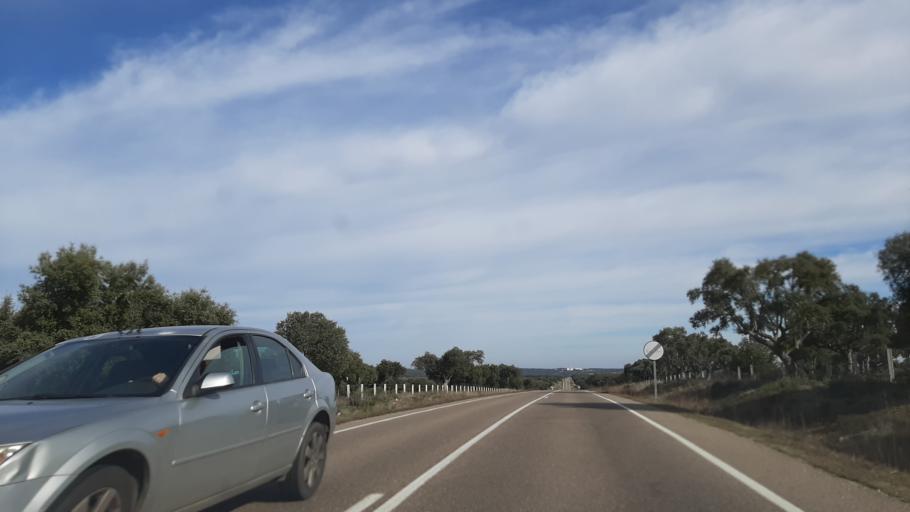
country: ES
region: Castille and Leon
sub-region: Provincia de Salamanca
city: Ledesma
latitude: 41.0897
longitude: -5.9511
